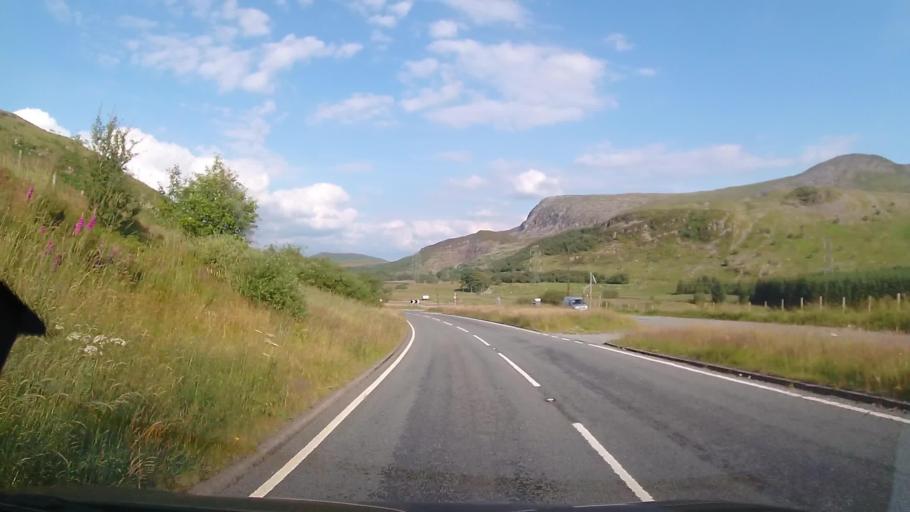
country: GB
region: Wales
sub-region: Conwy
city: Betws-y-Coed
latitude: 52.9396
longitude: -3.7639
